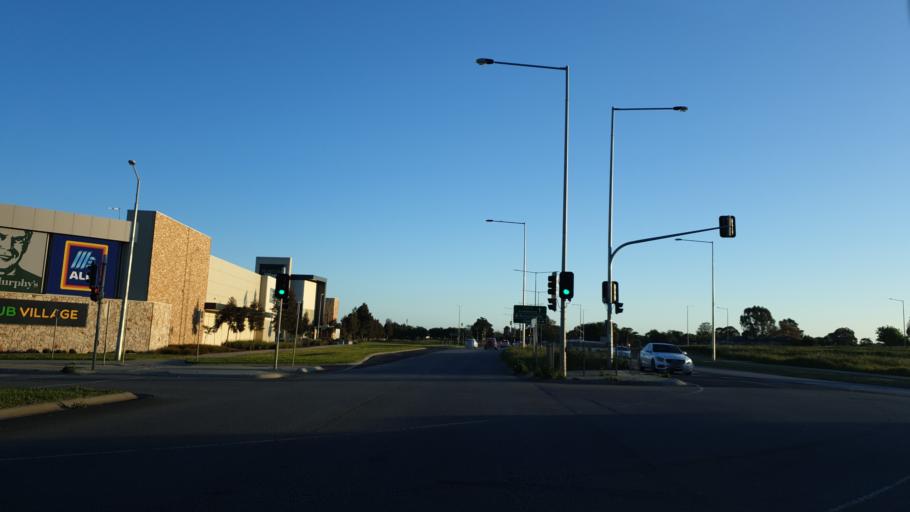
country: AU
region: Victoria
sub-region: Casey
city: Cranbourne
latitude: -38.0983
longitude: 145.2929
